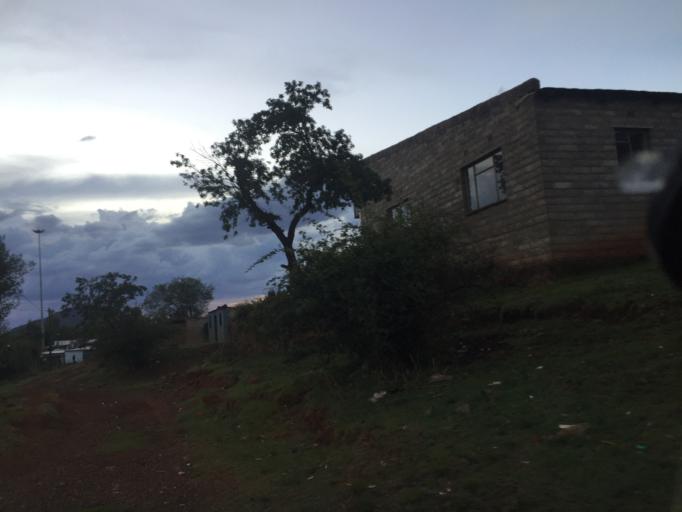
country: LS
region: Berea
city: Teyateyaneng
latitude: -29.1614
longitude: 28.0341
